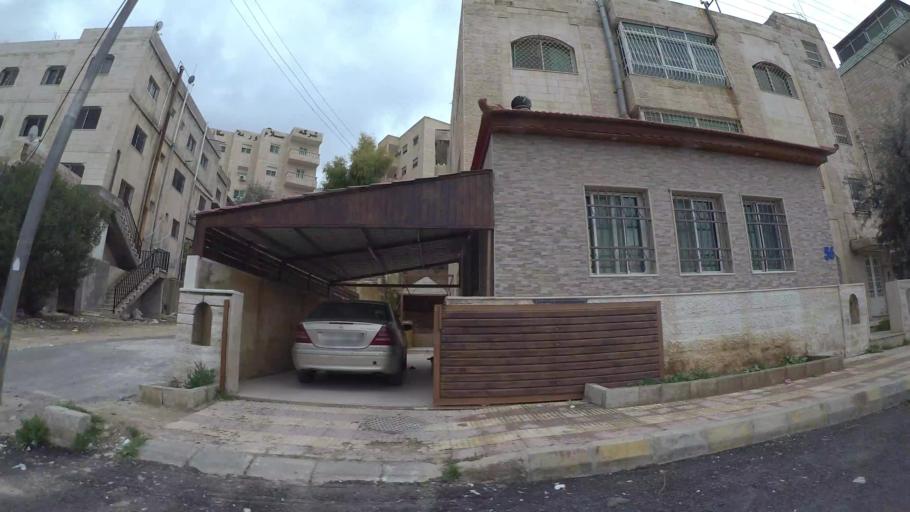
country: JO
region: Amman
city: Amman
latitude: 32.0049
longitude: 35.9500
